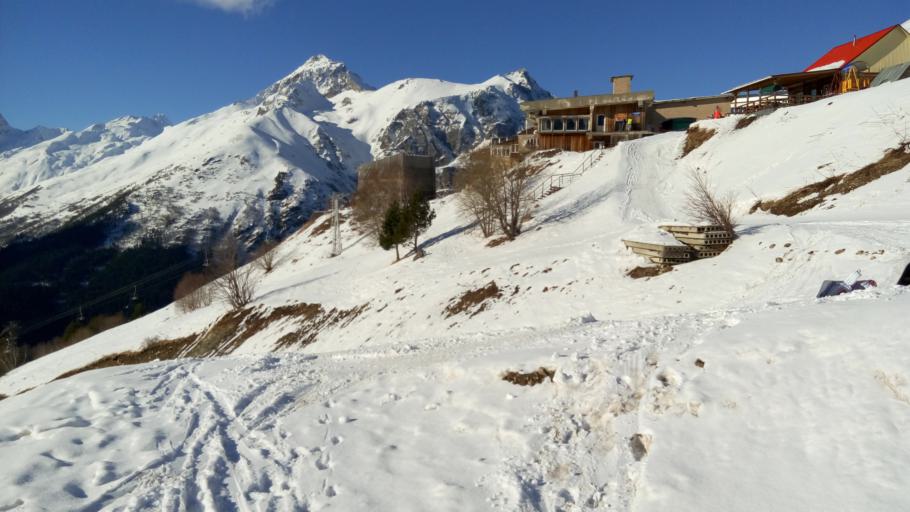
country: RU
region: Karachayevo-Cherkesiya
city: Teberda
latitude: 43.2897
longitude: 41.6485
